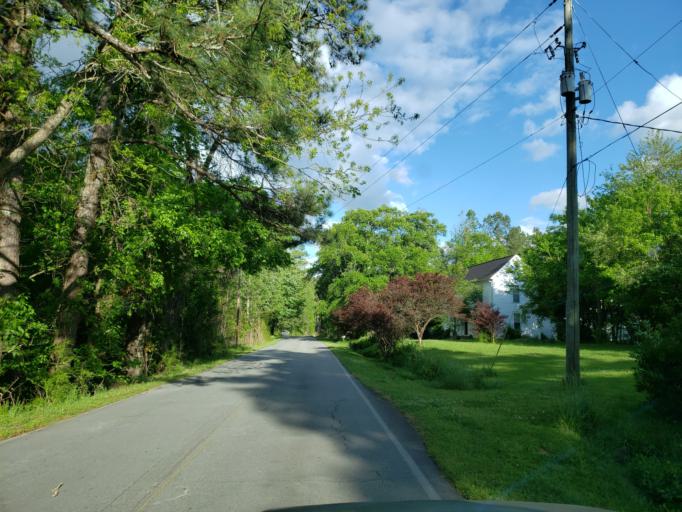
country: US
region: Georgia
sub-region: Haralson County
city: Tallapoosa
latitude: 33.7725
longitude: -85.3028
